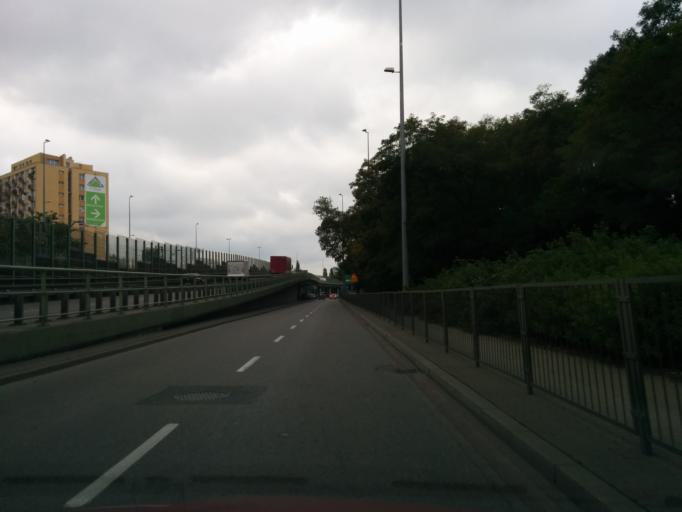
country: PL
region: Masovian Voivodeship
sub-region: Warszawa
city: Praga Polnoc
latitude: 52.2652
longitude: 21.0247
